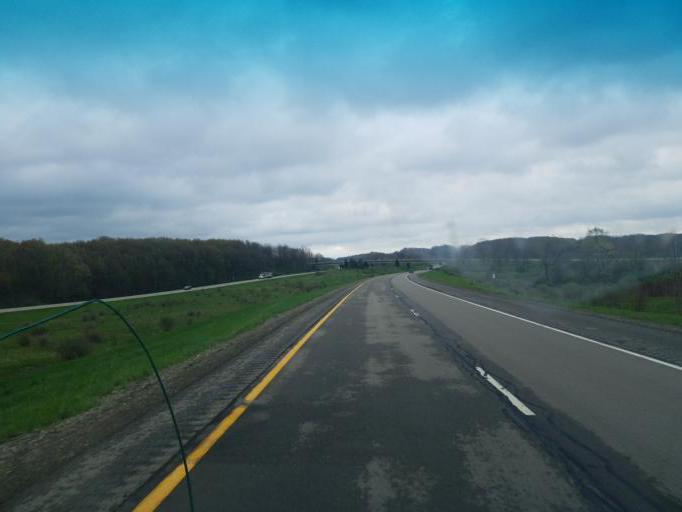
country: US
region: New York
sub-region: Chautauqua County
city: Clymer
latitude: 42.1472
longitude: -79.6588
